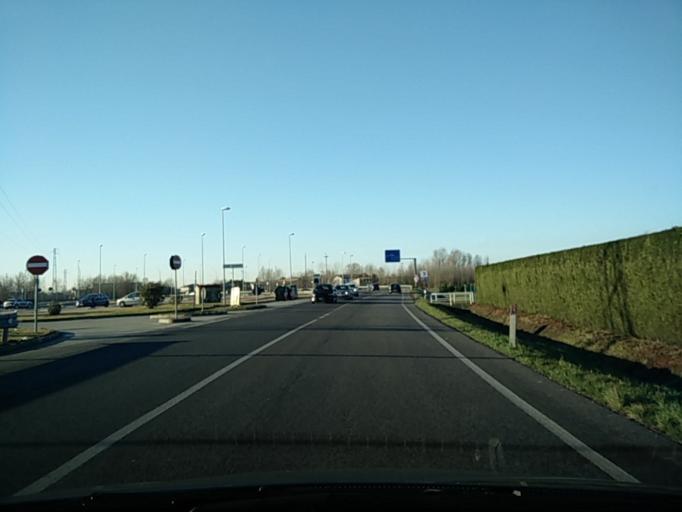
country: IT
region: Veneto
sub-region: Provincia di Venezia
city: Ballo
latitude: 45.4541
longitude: 12.0835
